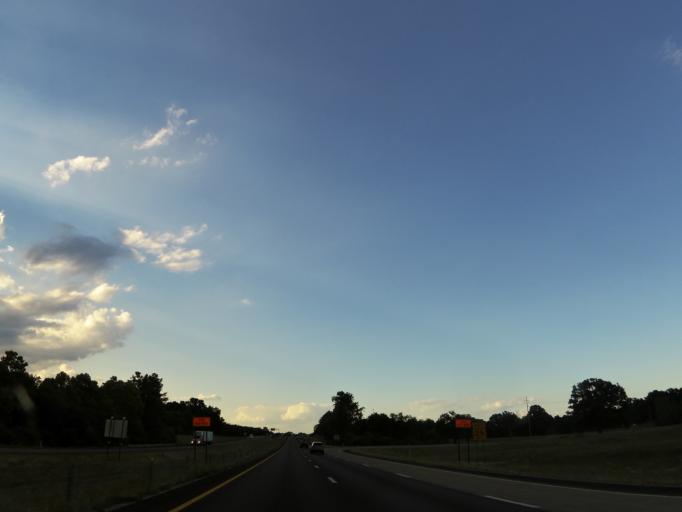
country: US
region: Tennessee
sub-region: Maury County
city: Spring Hill
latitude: 35.7418
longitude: -86.8724
